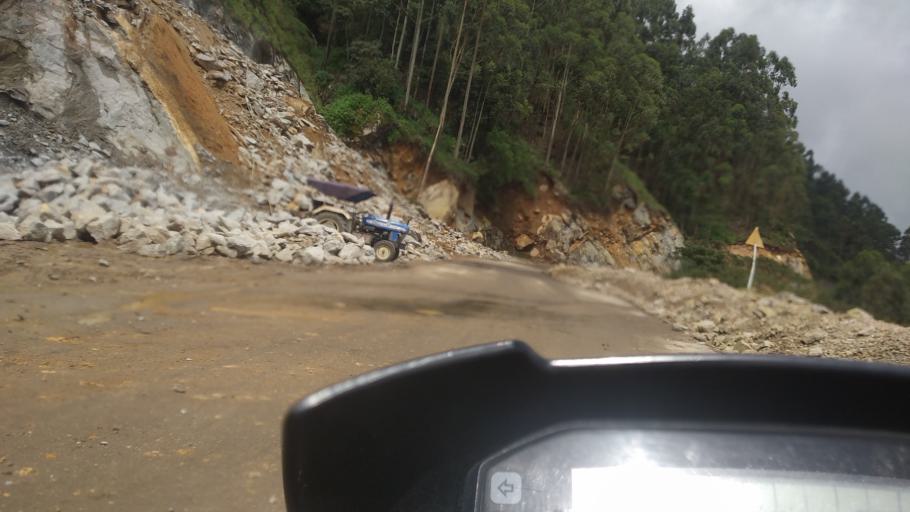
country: IN
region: Kerala
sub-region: Idukki
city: Munnar
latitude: 10.0369
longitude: 77.1323
